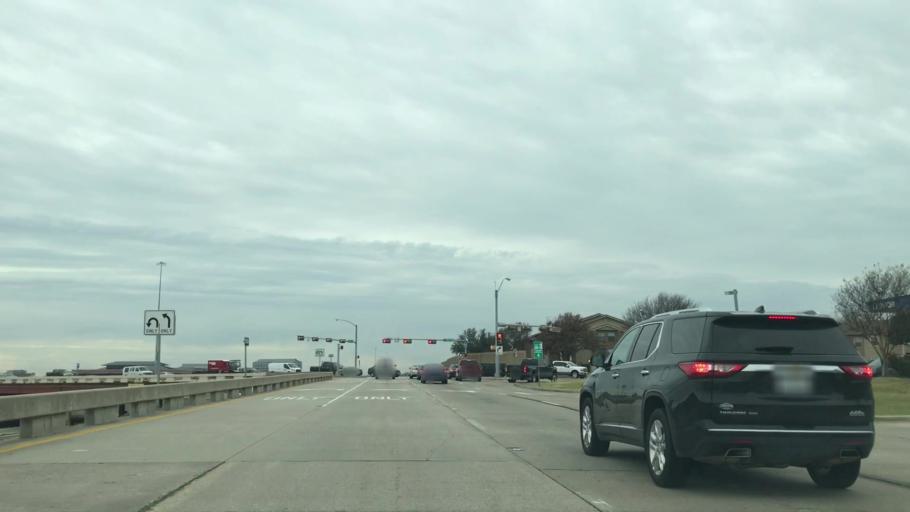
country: US
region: Texas
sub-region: Dallas County
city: Farmers Branch
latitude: 32.9060
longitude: -96.9580
